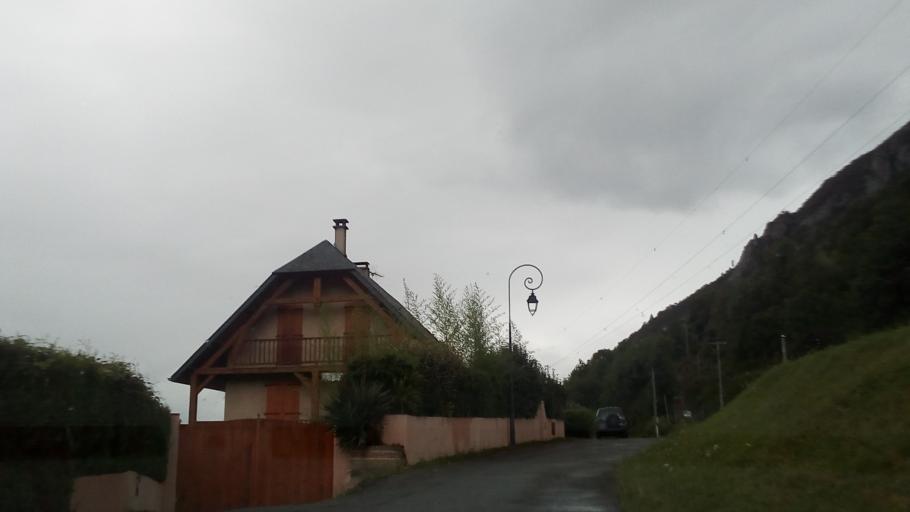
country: FR
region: Midi-Pyrenees
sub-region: Departement des Hautes-Pyrenees
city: Campan
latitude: 43.0211
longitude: 0.1773
